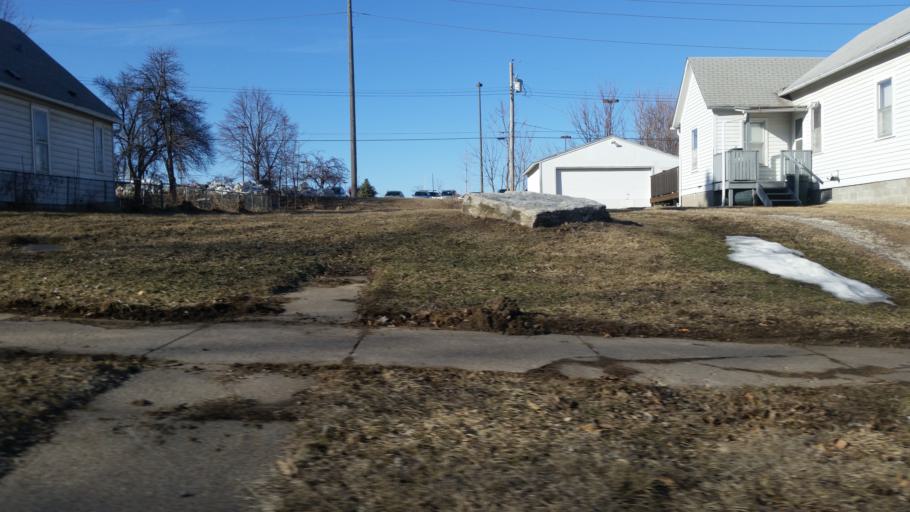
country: US
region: Nebraska
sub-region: Douglas County
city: Omaha
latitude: 41.2230
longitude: -95.9301
